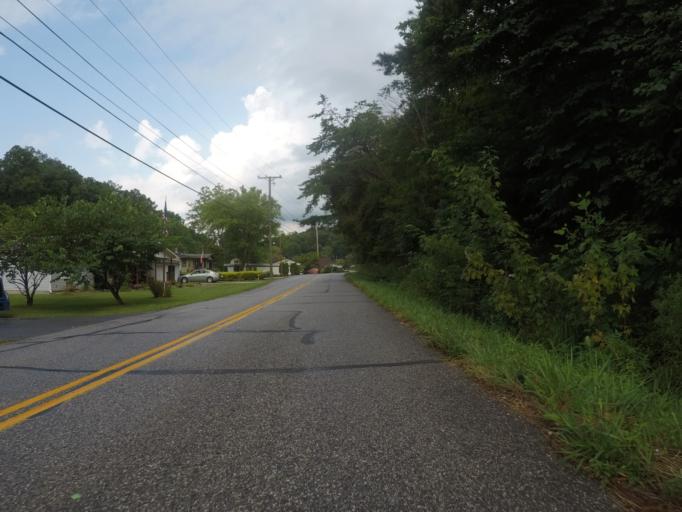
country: US
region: Kentucky
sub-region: Boyd County
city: Meads
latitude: 38.4155
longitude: -82.6889
